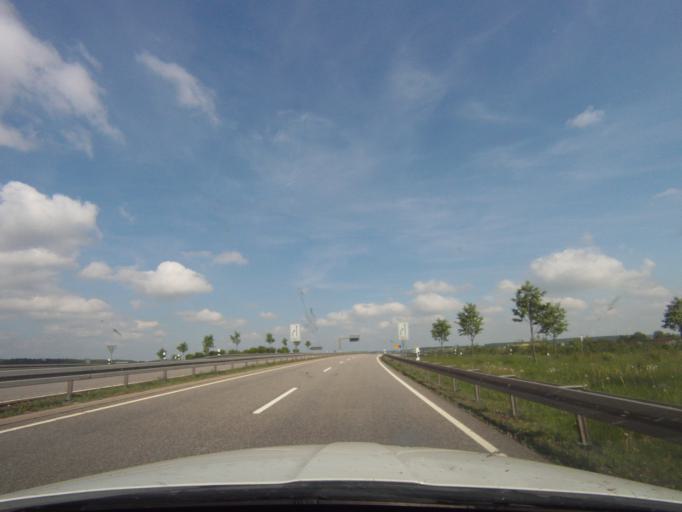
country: DE
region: Thuringia
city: Triptis
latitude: 50.7487
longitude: 11.8575
